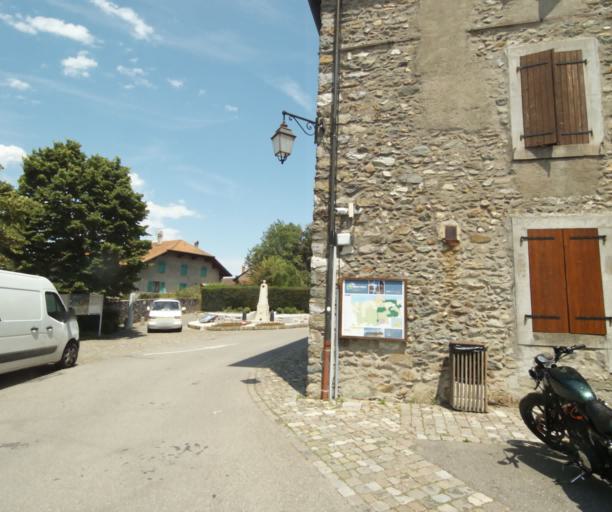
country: FR
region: Rhone-Alpes
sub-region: Departement de la Haute-Savoie
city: Messery
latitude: 46.3650
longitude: 6.3049
